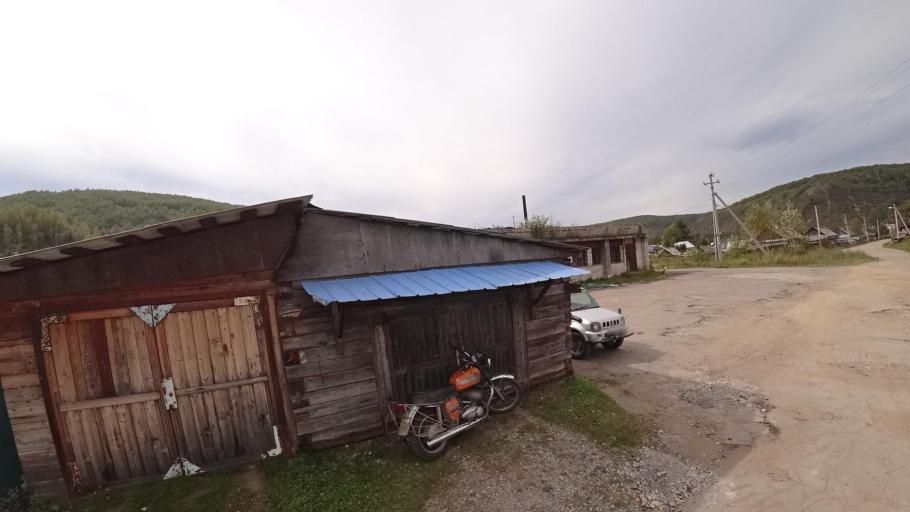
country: RU
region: Jewish Autonomous Oblast
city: Khingansk
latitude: 49.1242
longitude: 131.2035
